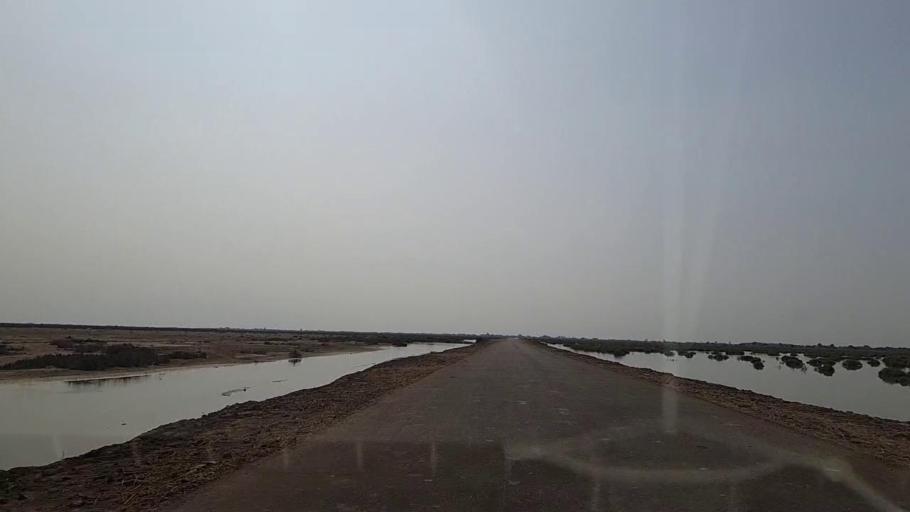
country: PK
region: Sindh
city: Chuhar Jamali
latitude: 24.2126
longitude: 67.8628
